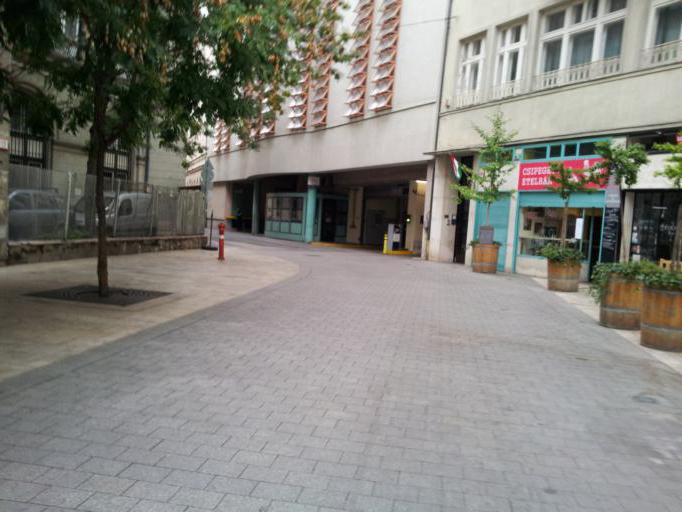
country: HU
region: Budapest
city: Budapest VIII. keruelet
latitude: 47.4910
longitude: 19.0610
